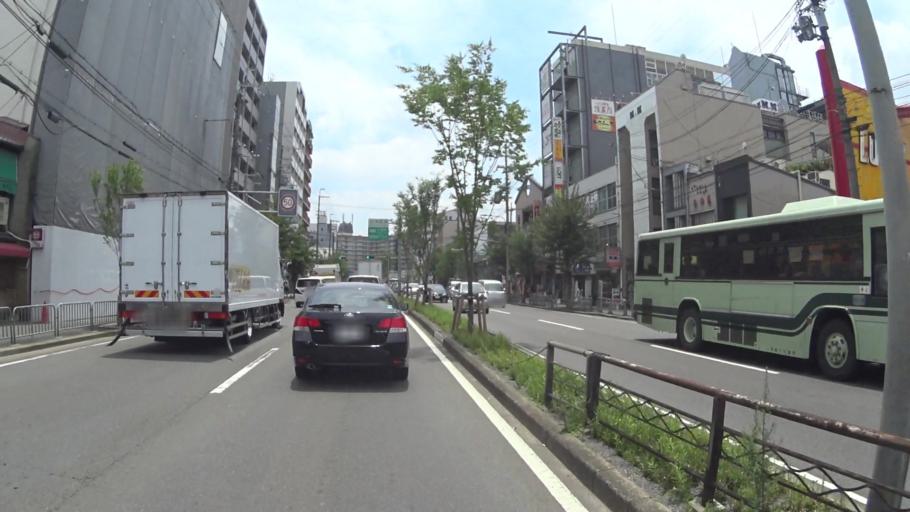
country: JP
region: Kyoto
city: Muko
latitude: 34.9807
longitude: 135.7328
